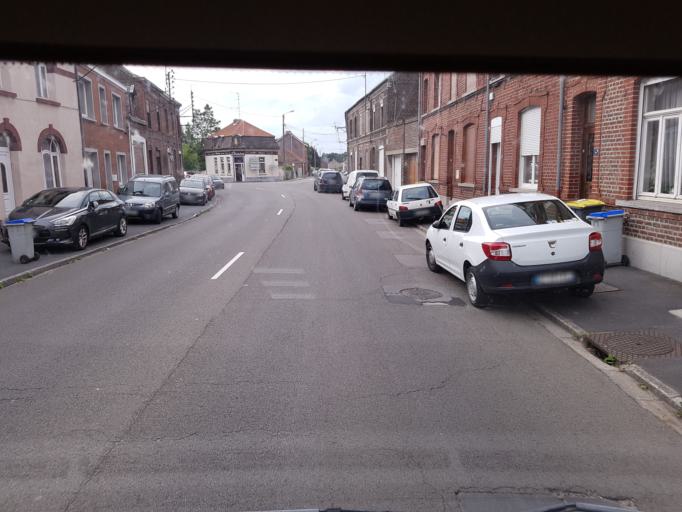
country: FR
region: Nord-Pas-de-Calais
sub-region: Departement du Nord
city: Conde-sur-l'Escaut
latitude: 50.4551
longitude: 3.5862
